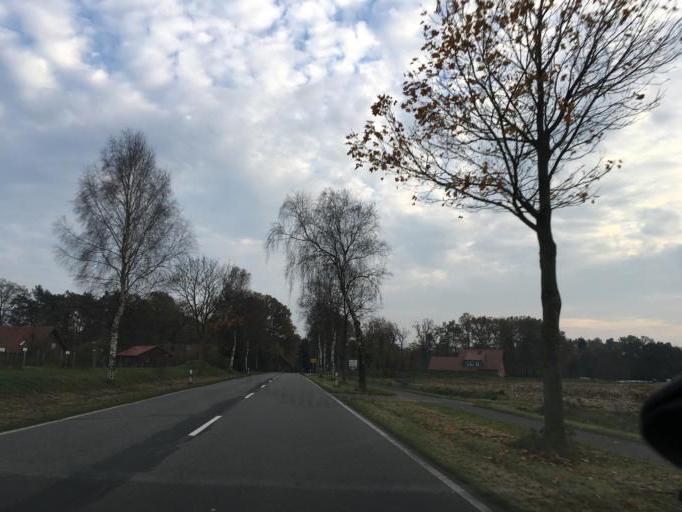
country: DE
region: Lower Saxony
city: Wietzendorf
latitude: 52.9478
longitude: 9.9802
